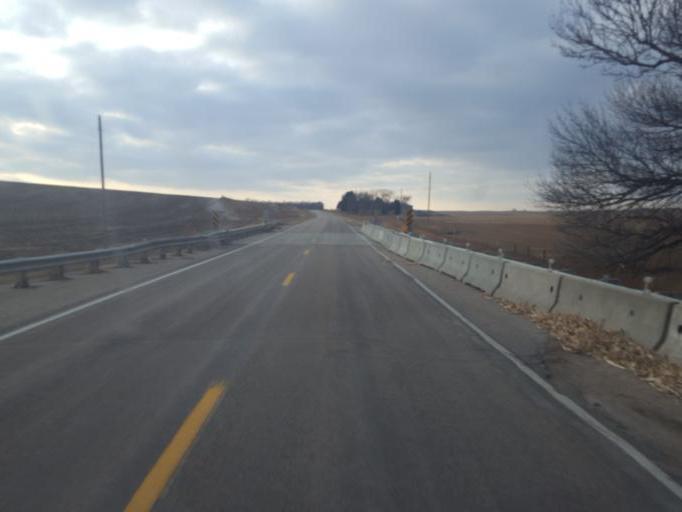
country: US
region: Nebraska
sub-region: Cedar County
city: Hartington
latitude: 42.6128
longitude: -97.4291
